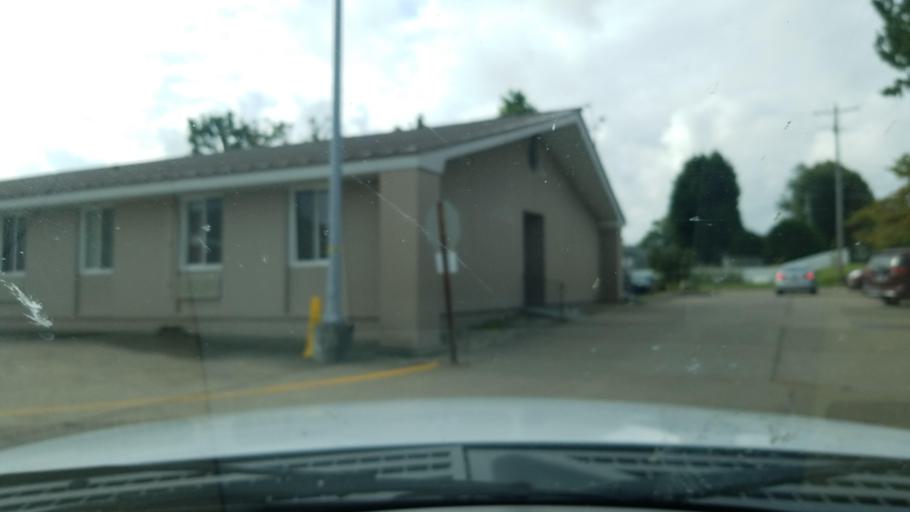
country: US
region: Illinois
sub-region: Saline County
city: Harrisburg
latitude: 37.7308
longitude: -88.5240
